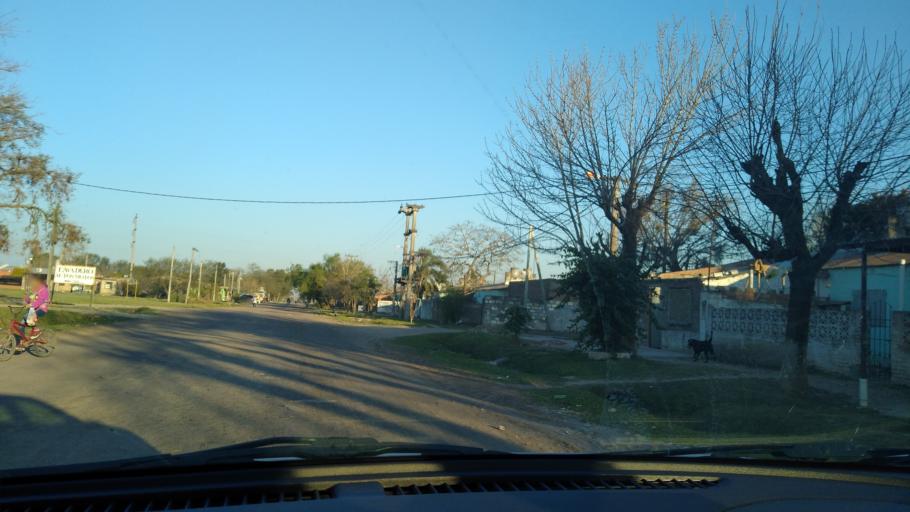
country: AR
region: Chaco
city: Puerto Vilelas
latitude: -27.5008
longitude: -58.9592
